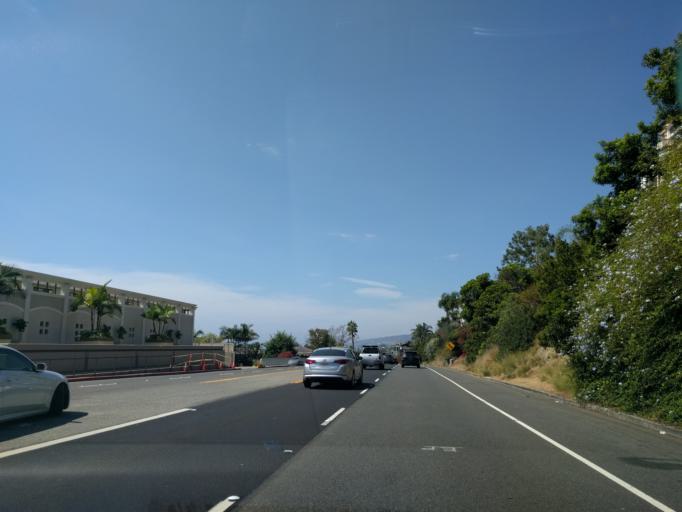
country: US
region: California
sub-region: Orange County
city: Laguna Niguel
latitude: 33.5061
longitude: -117.7475
